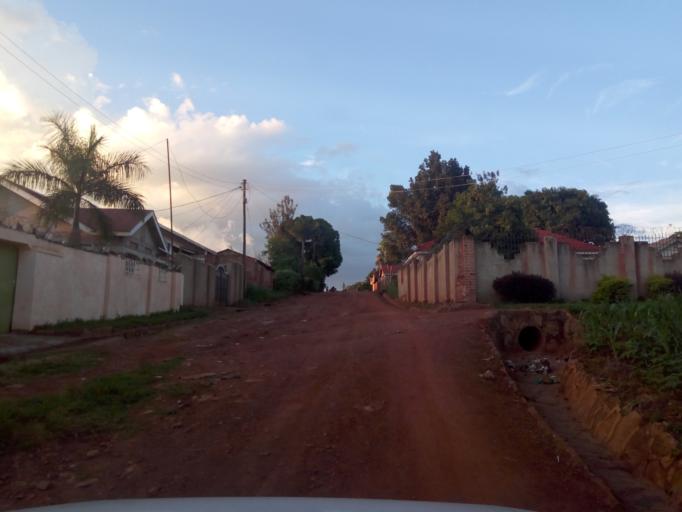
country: UG
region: Western Region
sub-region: Masindi District
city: Masindi
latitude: 1.6810
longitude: 31.7154
